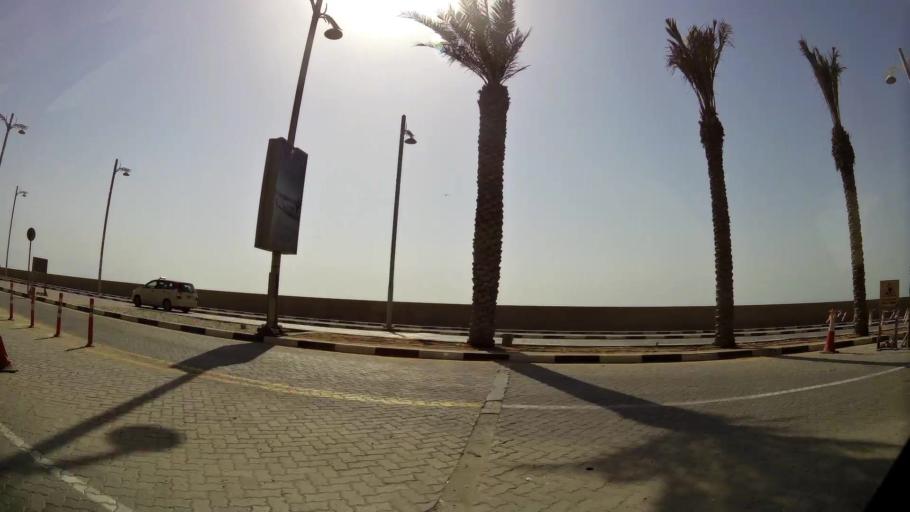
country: AE
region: Dubai
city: Dubai
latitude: 25.1263
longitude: 55.1123
